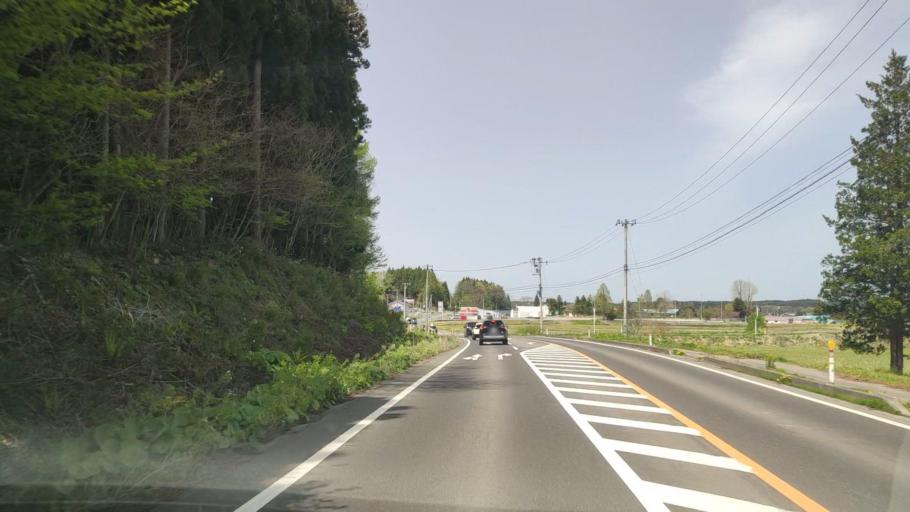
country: JP
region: Aomori
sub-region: Misawa Shi
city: Inuotose
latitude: 40.5859
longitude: 141.3550
